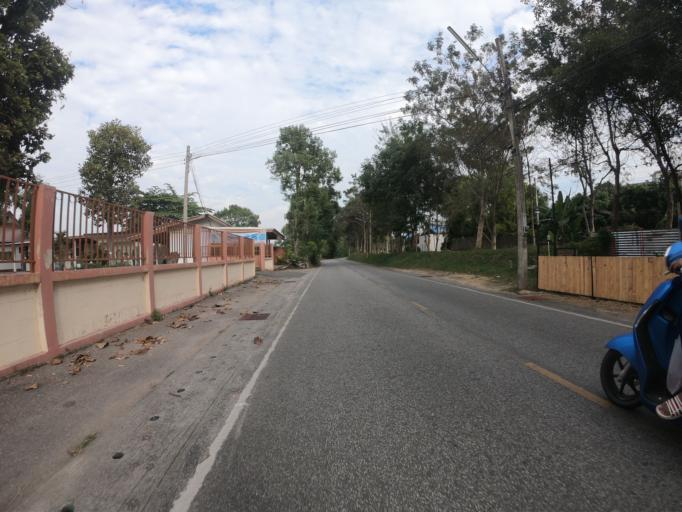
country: TH
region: Chiang Mai
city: Chiang Mai
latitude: 18.8133
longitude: 98.9785
